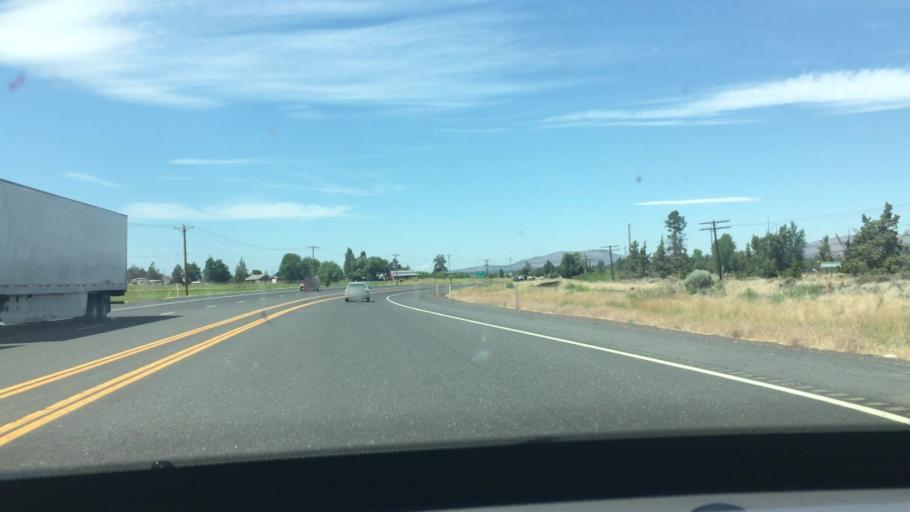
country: US
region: Oregon
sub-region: Deschutes County
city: Terrebonne
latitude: 44.3243
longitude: -121.1751
